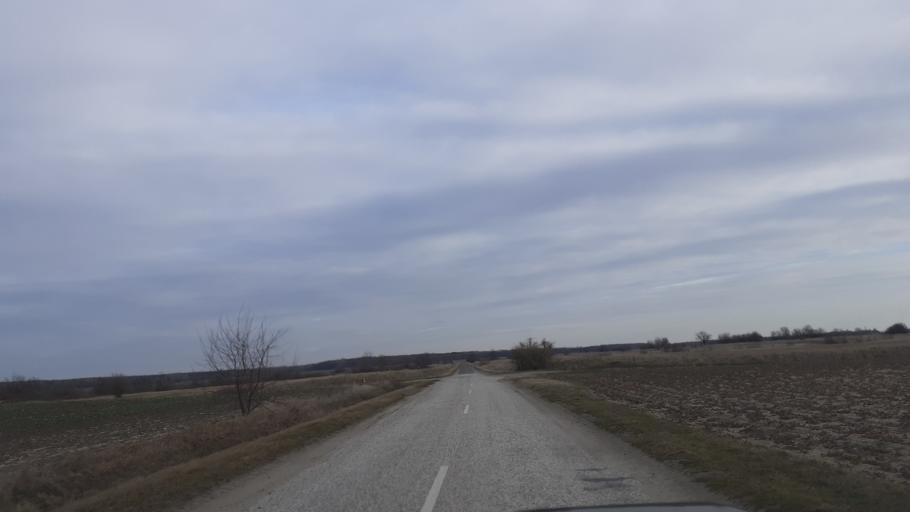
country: HU
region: Fejer
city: Szabadbattyan
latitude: 47.1081
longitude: 18.4329
